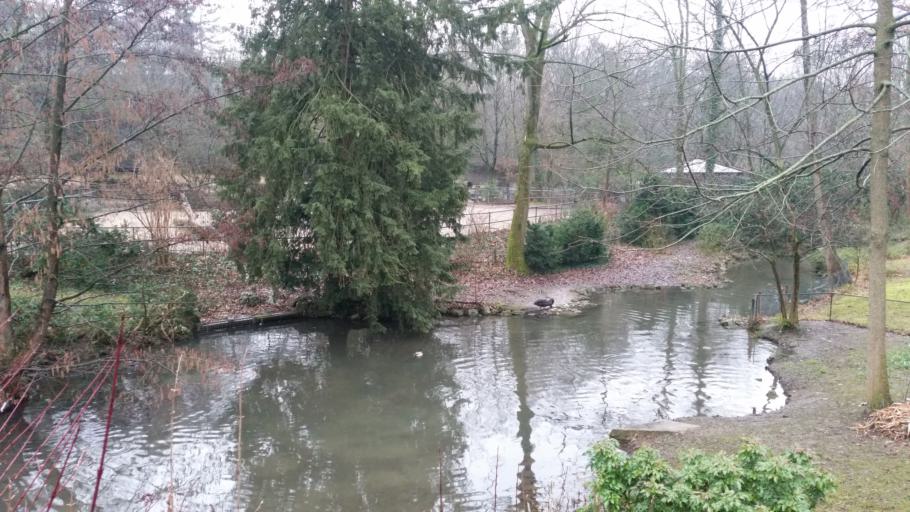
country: CH
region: Basel-City
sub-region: Basel-Stadt
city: Basel
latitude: 47.5480
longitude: 7.5802
